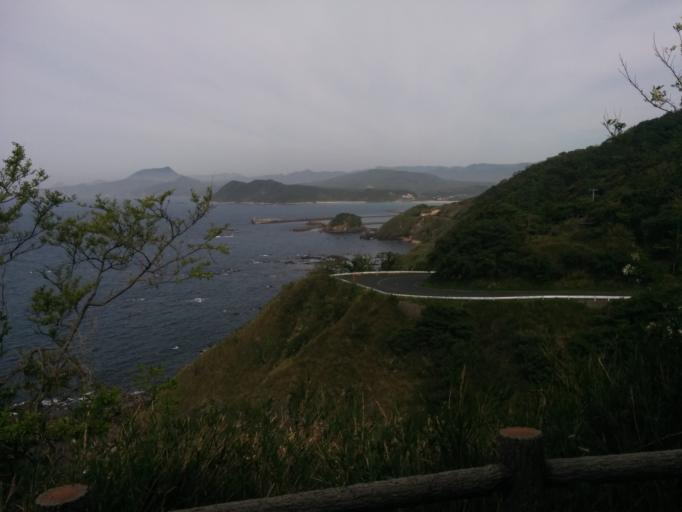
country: JP
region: Hyogo
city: Toyooka
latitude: 35.6930
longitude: 135.0031
